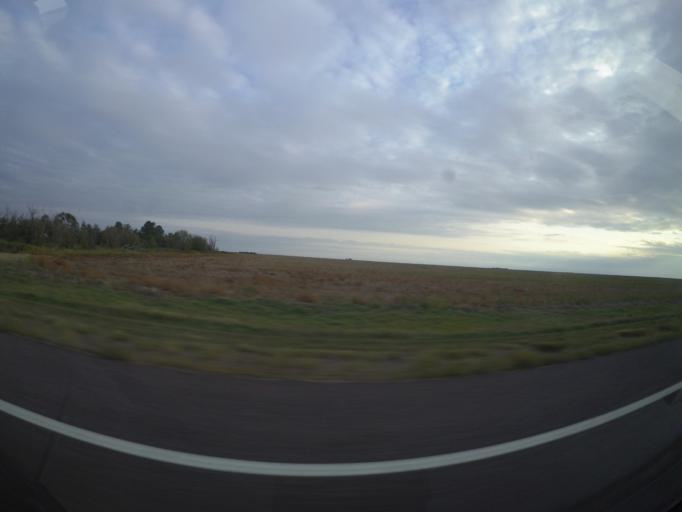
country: US
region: Colorado
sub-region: Yuma County
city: Wray
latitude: 39.7462
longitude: -102.1760
